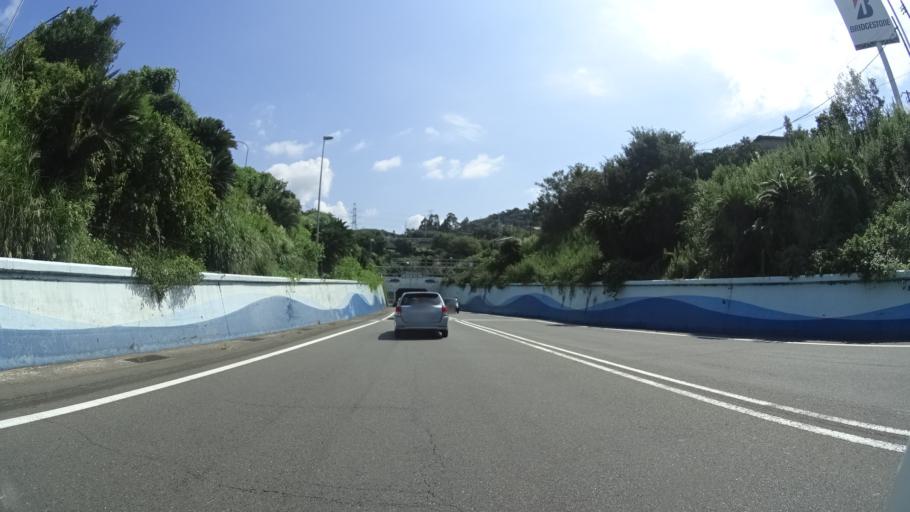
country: JP
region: Yamaguchi
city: Shimonoseki
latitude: 33.9761
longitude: 130.9469
